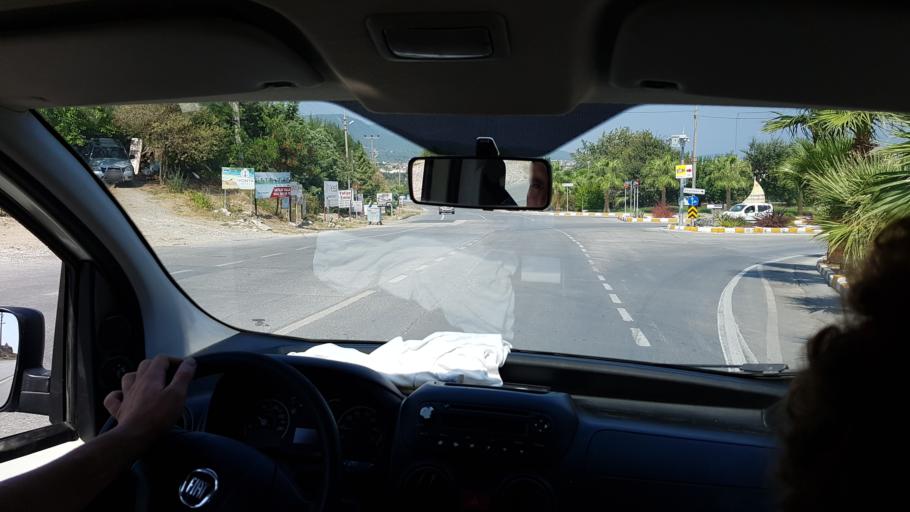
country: TR
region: Izmir
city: Urla
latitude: 38.3791
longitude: 26.7588
